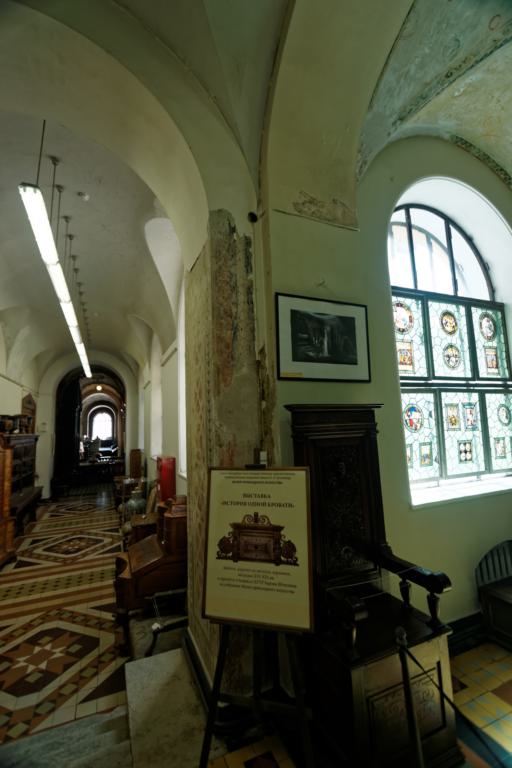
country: RU
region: St.-Petersburg
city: Centralniy
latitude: 59.9432
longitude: 30.3409
